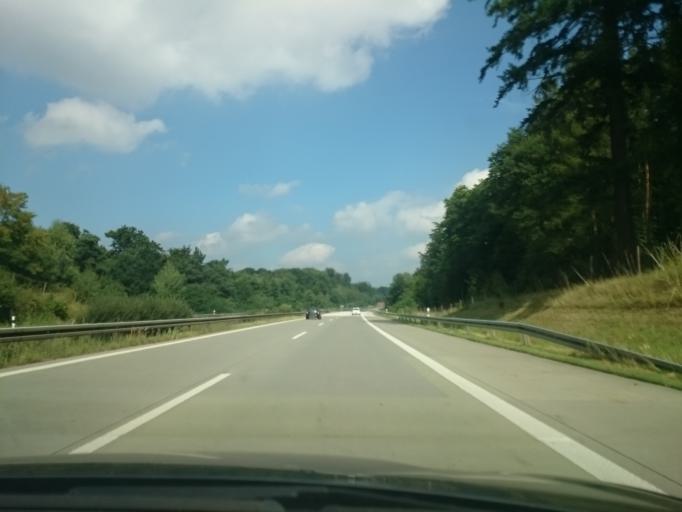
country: DE
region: Brandenburg
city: Rudnitz
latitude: 52.7580
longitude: 13.5453
